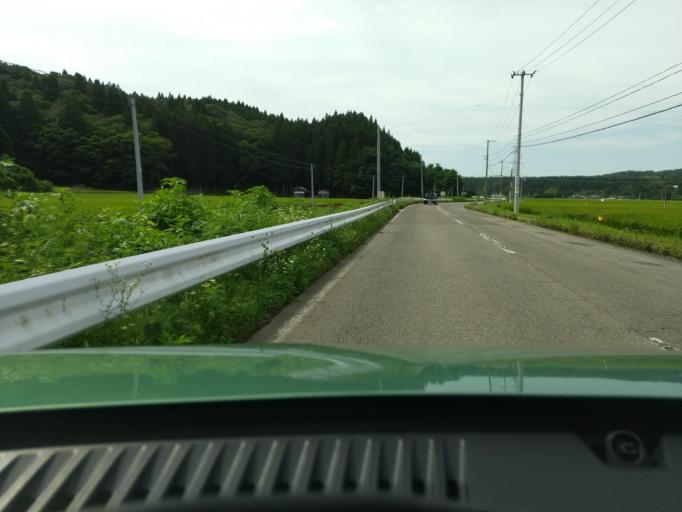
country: JP
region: Akita
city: Akita
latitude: 39.7867
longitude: 140.1220
